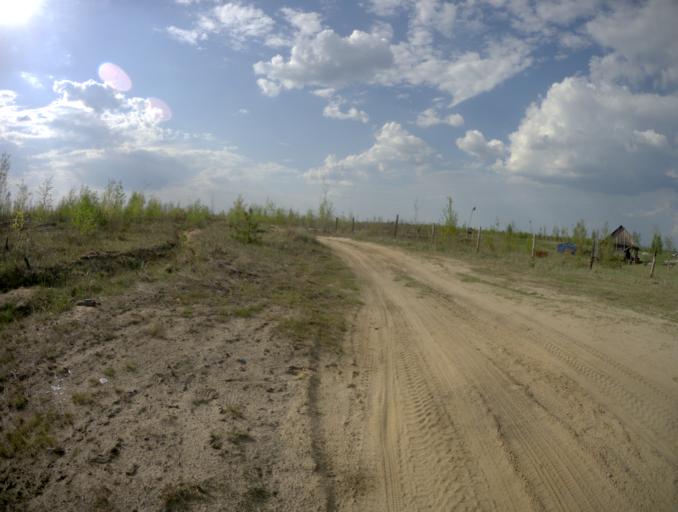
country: RU
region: Ivanovo
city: Talitsy
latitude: 56.4174
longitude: 42.2769
